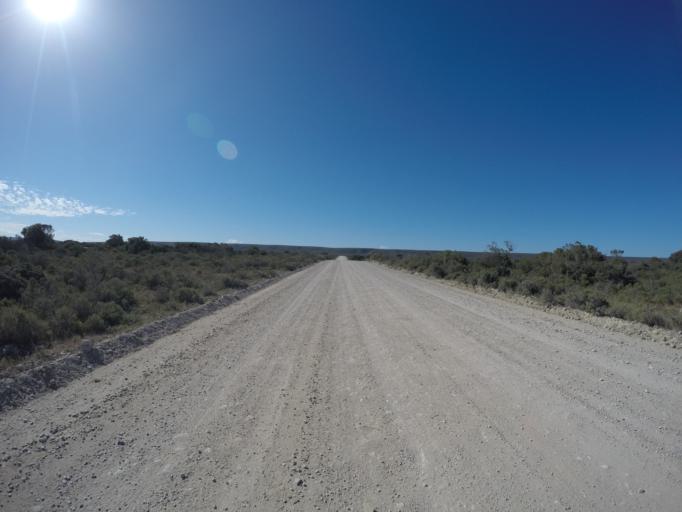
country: ZA
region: Western Cape
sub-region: Overberg District Municipality
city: Bredasdorp
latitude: -34.4539
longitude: 20.4243
